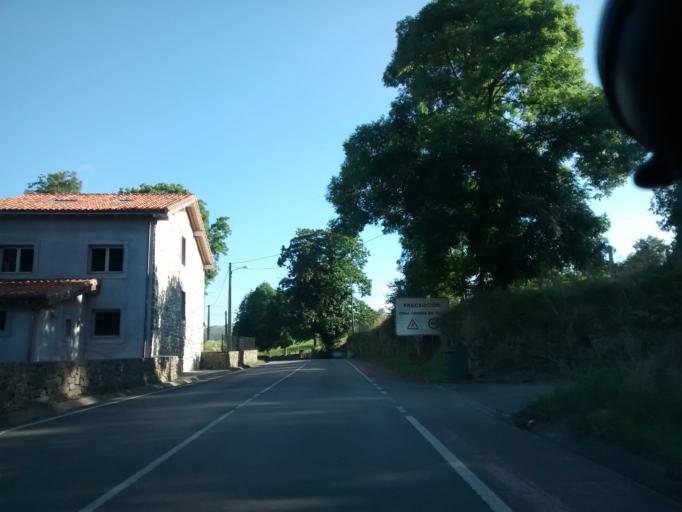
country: ES
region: Cantabria
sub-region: Provincia de Cantabria
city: Entrambasaguas
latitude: 43.3566
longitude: -3.7032
